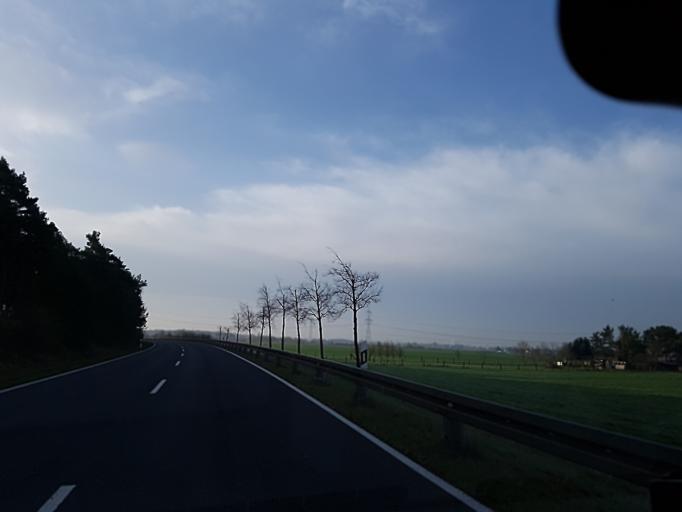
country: DE
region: Saxony
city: Riesa
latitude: 51.3434
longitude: 13.2985
